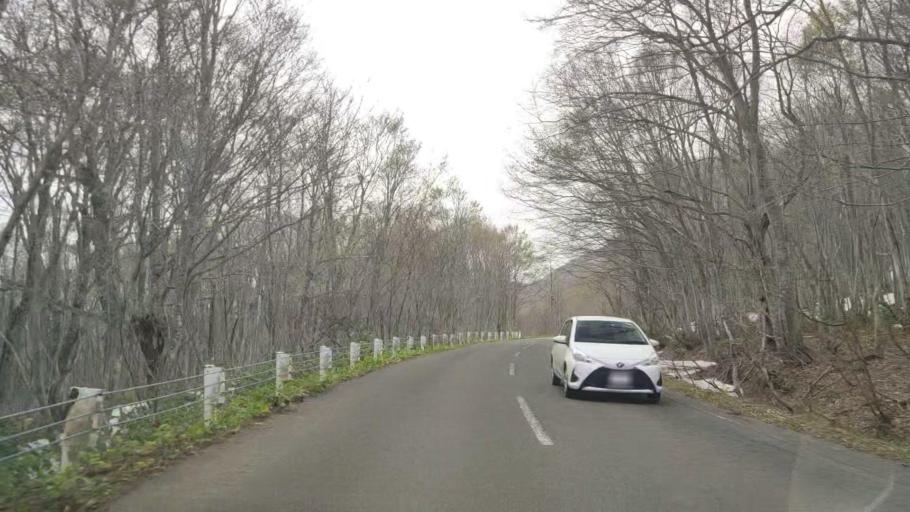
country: JP
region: Aomori
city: Aomori Shi
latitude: 40.6602
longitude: 140.9618
